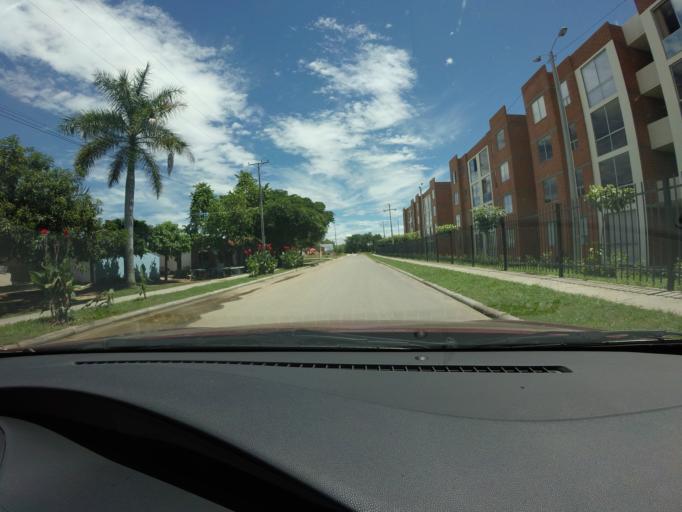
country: CO
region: Cundinamarca
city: Ricaurte
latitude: 4.2712
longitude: -74.7751
